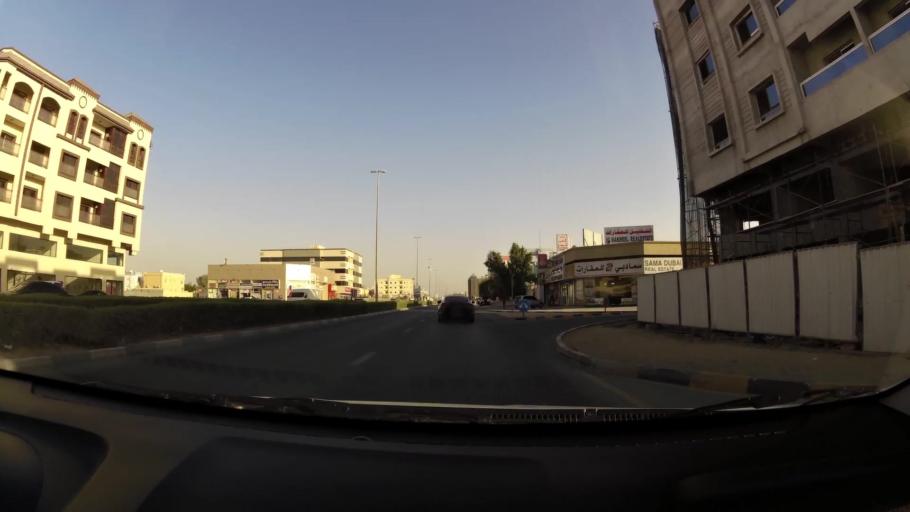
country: AE
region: Ajman
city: Ajman
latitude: 25.3877
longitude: 55.5061
